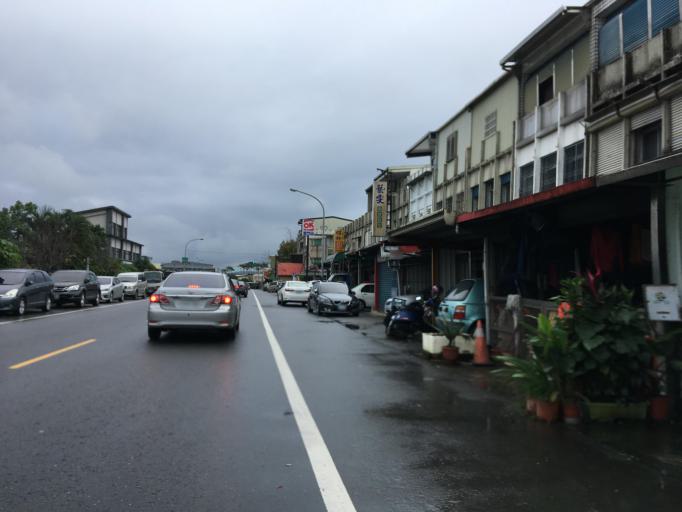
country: TW
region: Taiwan
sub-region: Yilan
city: Yilan
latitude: 24.6567
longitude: 121.7596
